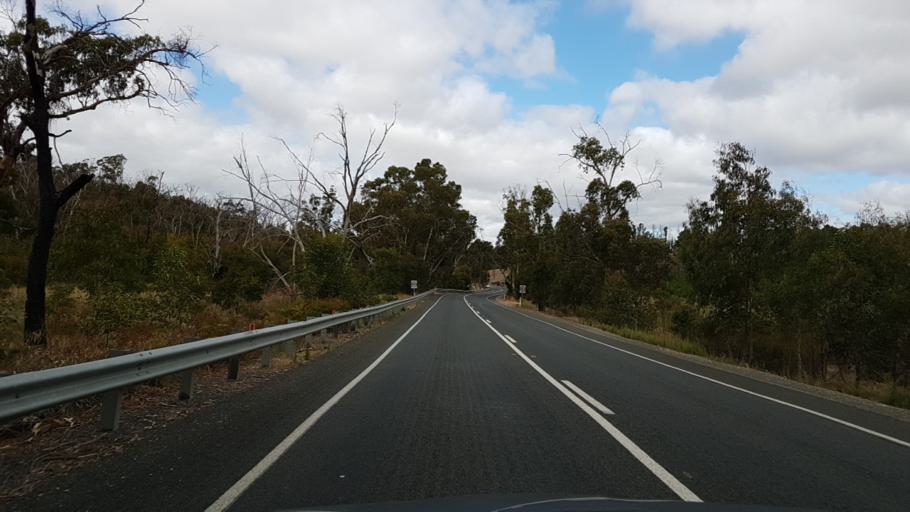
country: AU
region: South Australia
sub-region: Adelaide Hills
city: Gumeracha
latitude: -34.7715
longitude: 138.8301
